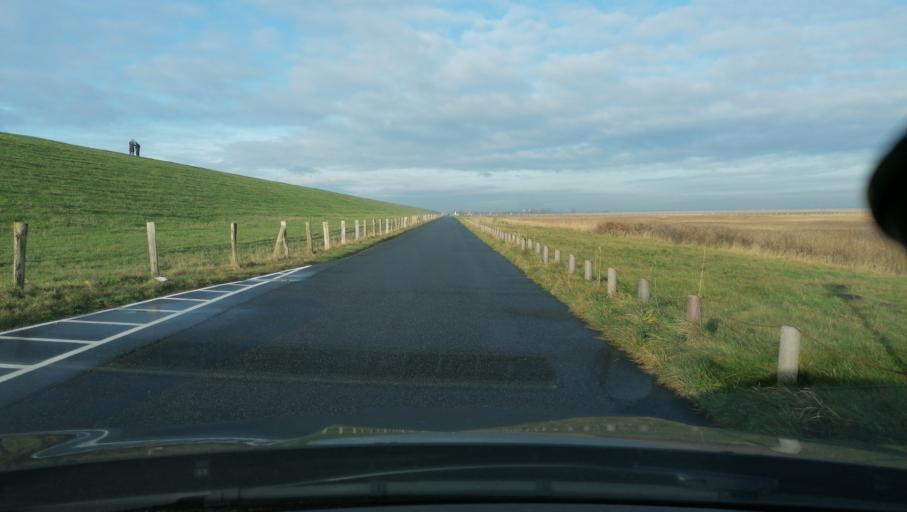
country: DE
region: Schleswig-Holstein
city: Friedrichsgabekoog
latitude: 54.0971
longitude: 8.9483
